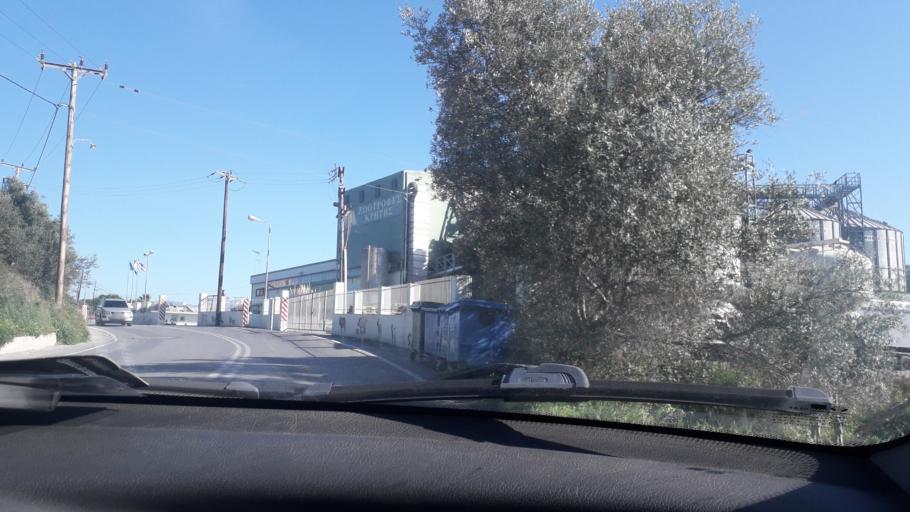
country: GR
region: Crete
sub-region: Nomos Rethymnis
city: Rethymno
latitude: 35.3593
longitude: 24.5500
